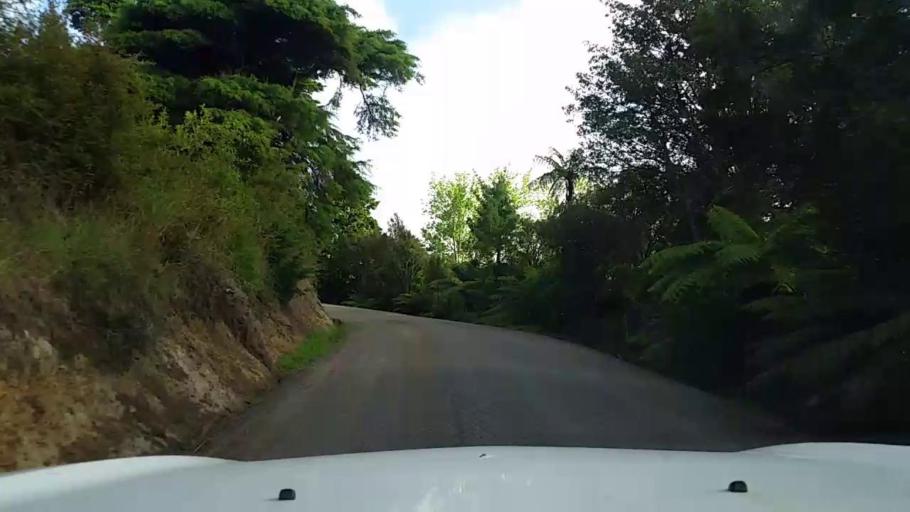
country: NZ
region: Northland
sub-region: Whangarei
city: Maungatapere
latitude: -35.6766
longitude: 174.1769
